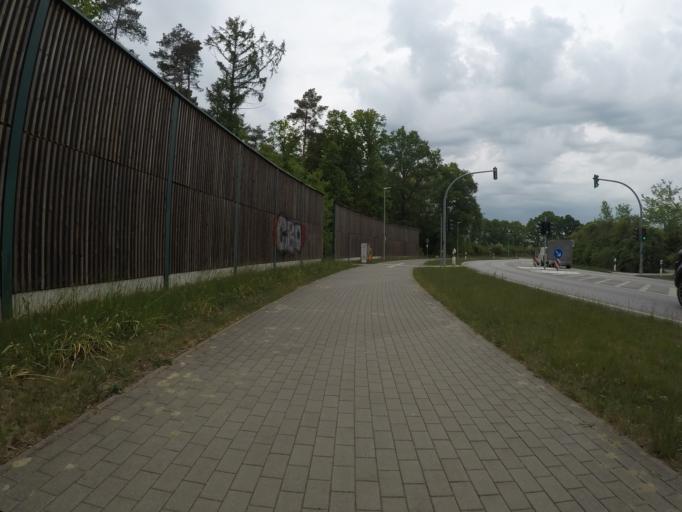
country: DE
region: Schleswig-Holstein
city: Norderstedt
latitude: 53.7222
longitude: 9.9818
